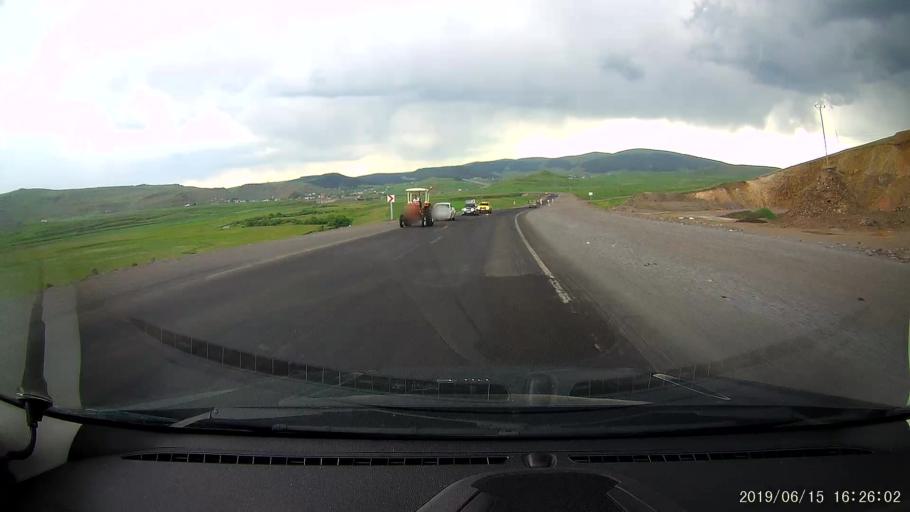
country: TR
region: Ardahan
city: Hanak
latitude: 41.1465
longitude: 42.8644
